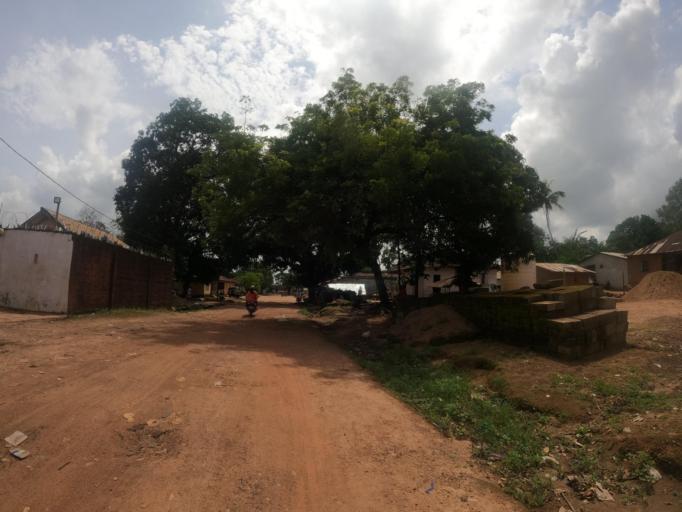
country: SL
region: Northern Province
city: Makeni
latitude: 8.8910
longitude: -12.0606
